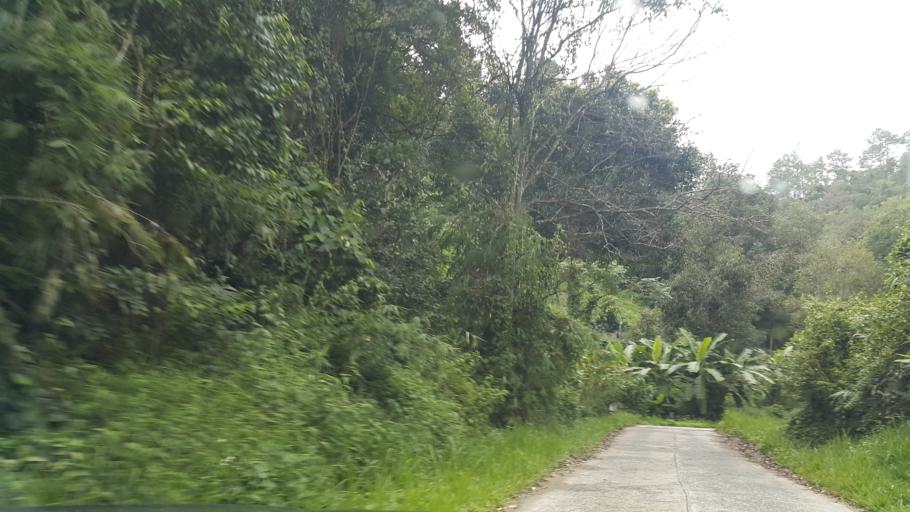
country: TH
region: Lampang
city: Wang Nuea
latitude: 19.0785
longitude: 99.3864
